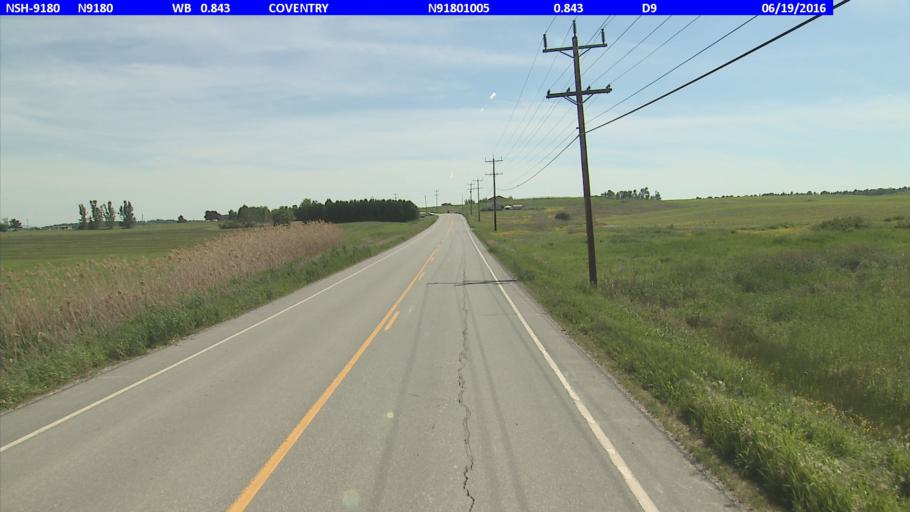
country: US
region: Vermont
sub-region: Orleans County
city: Newport
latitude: 44.9009
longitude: -72.2242
